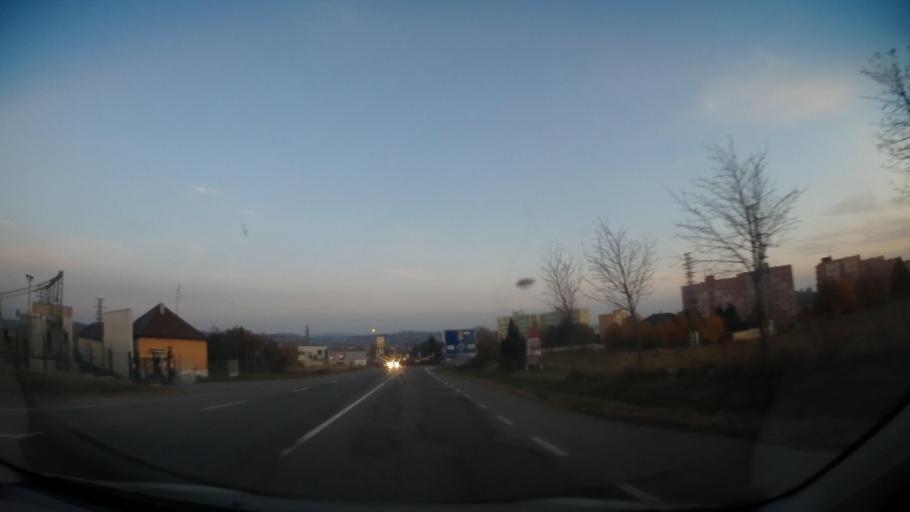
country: CZ
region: Vysocina
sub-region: Okres Pelhrimov
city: Pelhrimov
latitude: 49.4401
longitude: 15.2079
